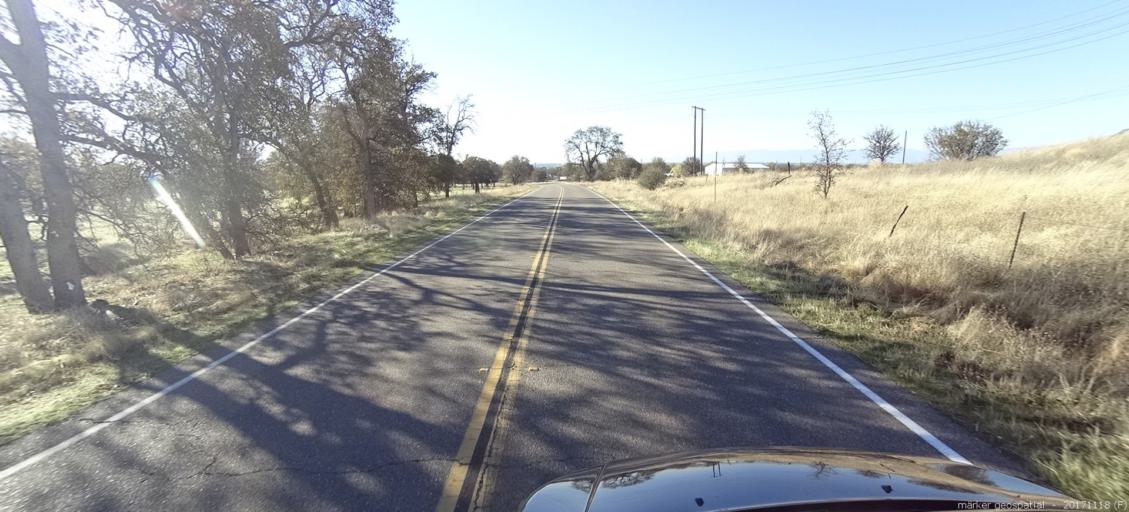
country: US
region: California
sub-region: Shasta County
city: Cottonwood
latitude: 40.4044
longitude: -122.2729
